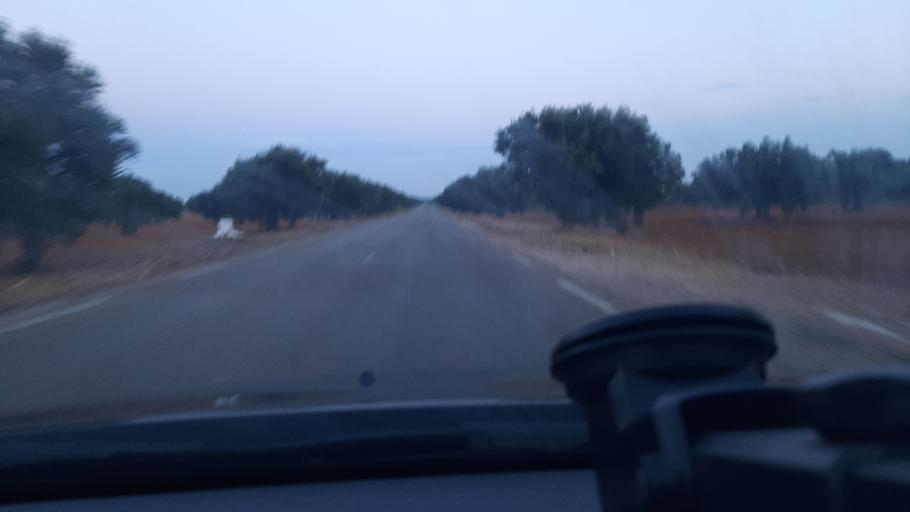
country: TN
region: Al Mahdiyah
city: Shurban
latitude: 35.0318
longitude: 10.4992
